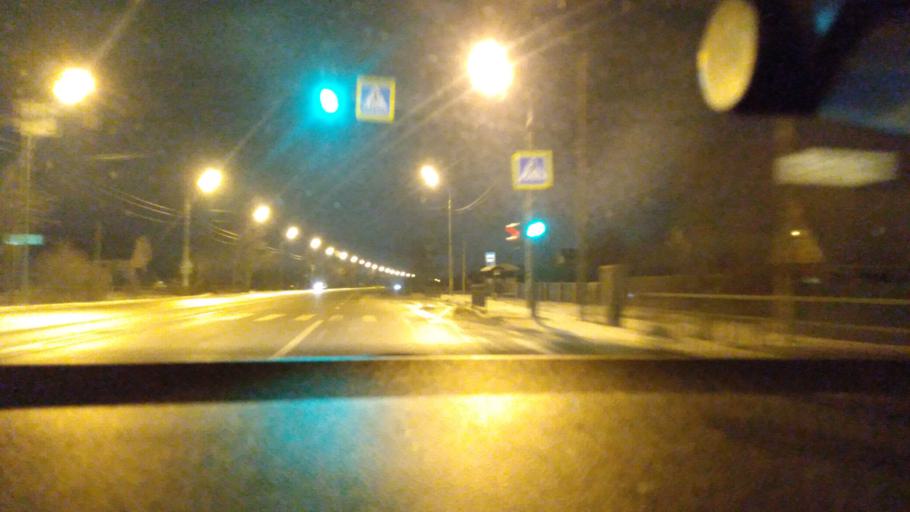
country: RU
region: Moskovskaya
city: Bronnitsy
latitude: 55.3977
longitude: 38.3172
